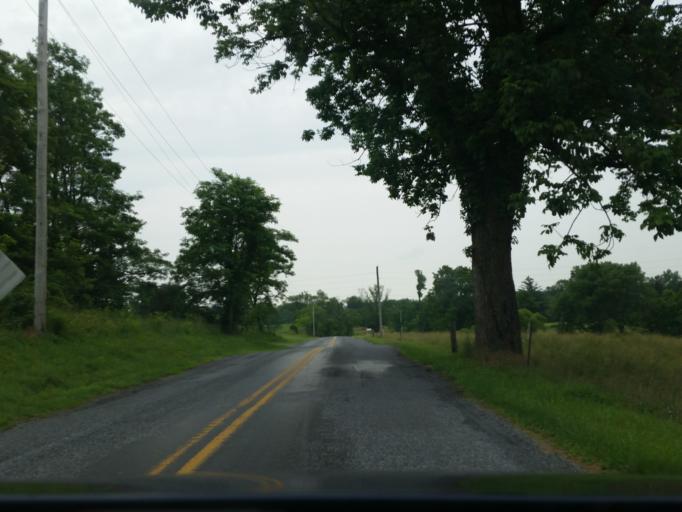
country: US
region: Pennsylvania
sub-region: Lebanon County
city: Palmyra
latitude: 40.3988
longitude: -76.6407
